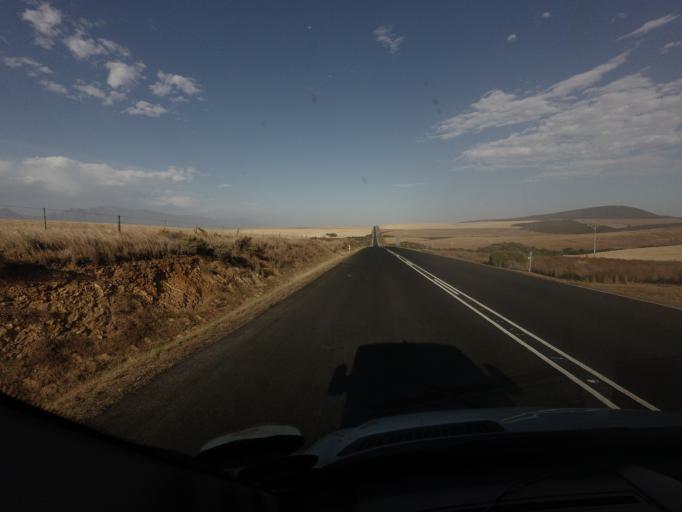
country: ZA
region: Western Cape
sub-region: Overberg District Municipality
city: Swellendam
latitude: -34.1059
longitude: 20.2653
